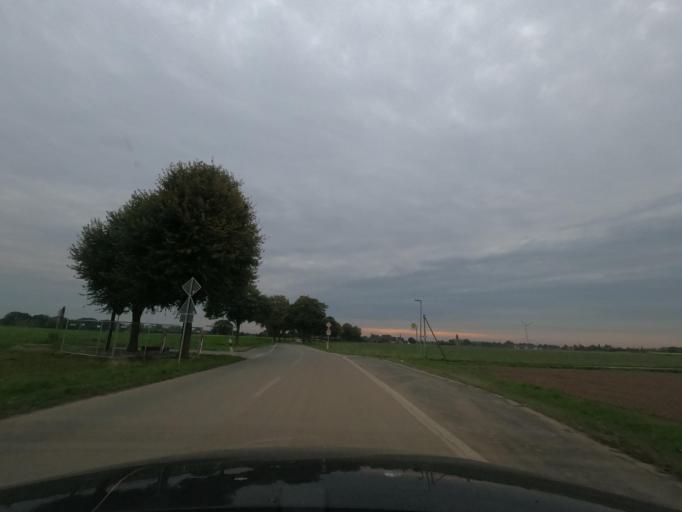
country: DE
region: North Rhine-Westphalia
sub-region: Regierungsbezirk Munster
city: Isselburg
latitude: 51.7866
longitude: 6.4458
